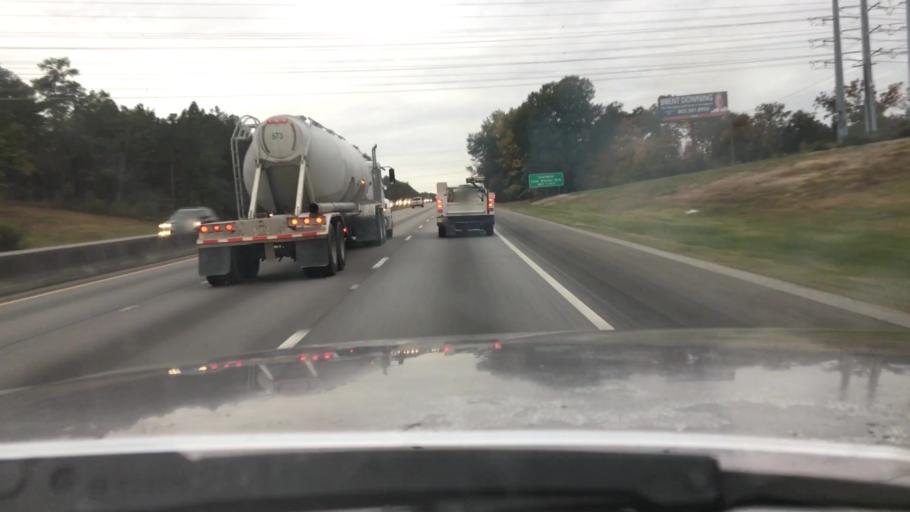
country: US
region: South Carolina
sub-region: Lexington County
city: Saint Andrews
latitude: 34.0216
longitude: -81.1335
